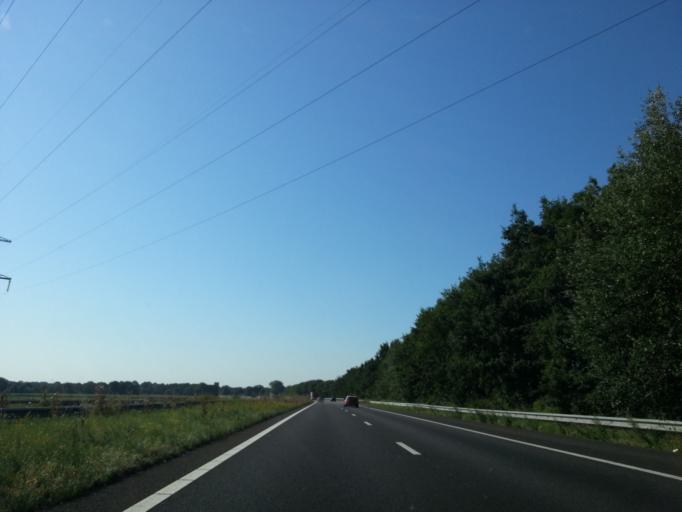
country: NL
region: Limburg
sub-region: Gemeente Nederweert
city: Nederweert
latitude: 51.2693
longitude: 5.7406
